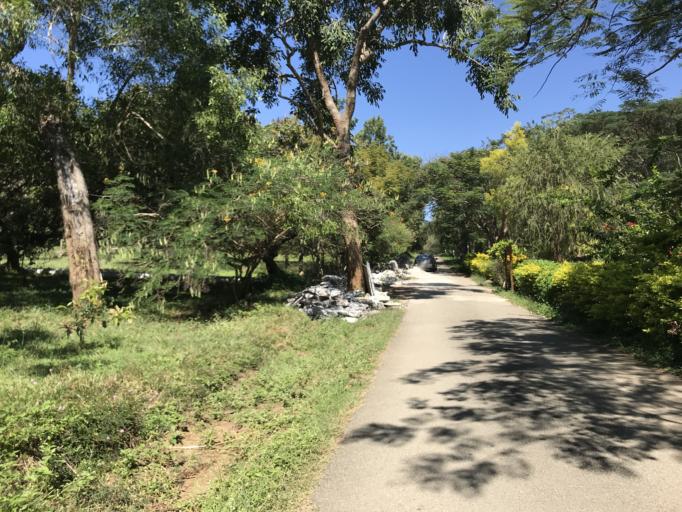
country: IN
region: Karnataka
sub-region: Mysore
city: Sargur
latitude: 11.9389
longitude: 76.2703
